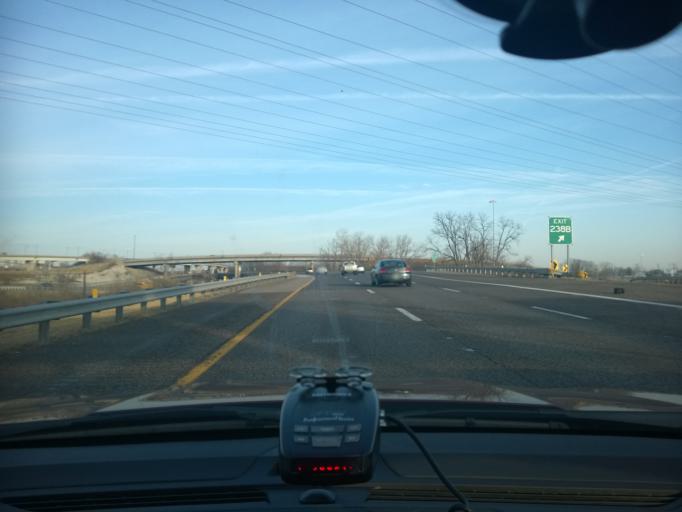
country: US
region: Missouri
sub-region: Saint Louis County
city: Saint Johns
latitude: 38.7296
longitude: -90.3310
